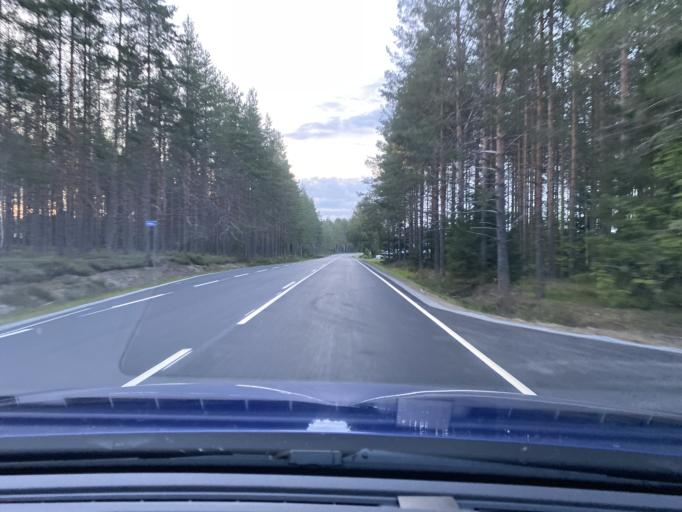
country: FI
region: Satakunta
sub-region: Pohjois-Satakunta
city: Honkajoki
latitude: 62.0627
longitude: 22.2490
